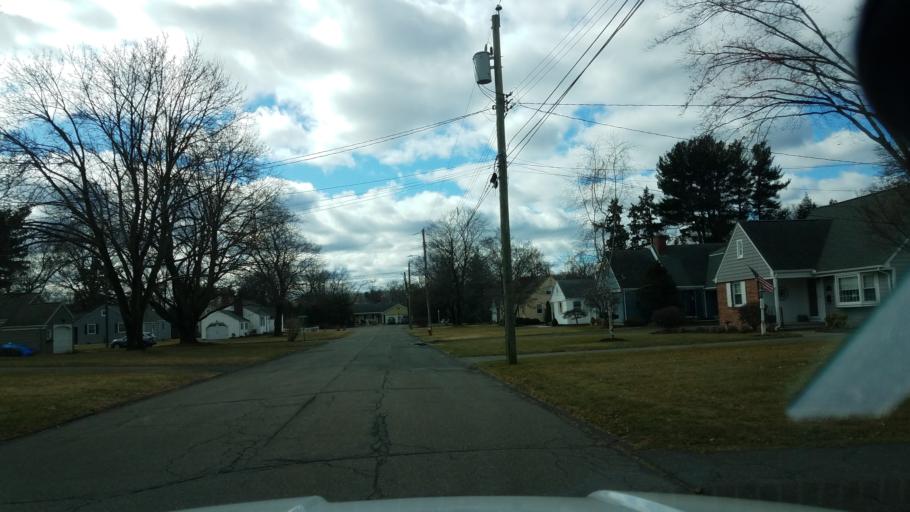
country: US
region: Connecticut
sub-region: Hartford County
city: Wethersfield
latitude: 41.7062
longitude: -72.6559
